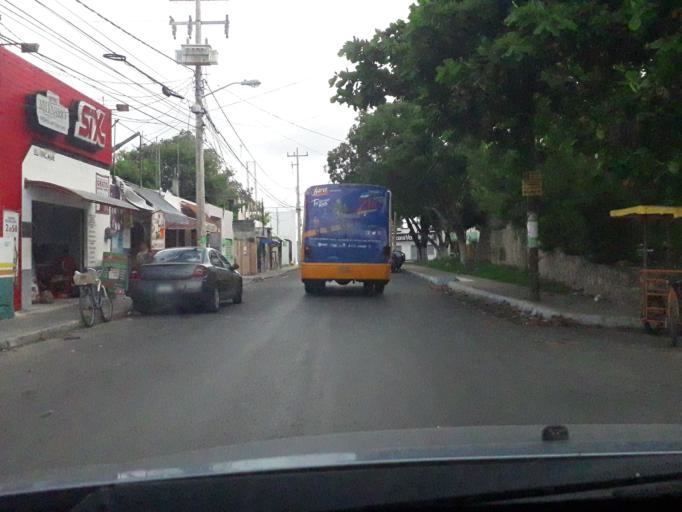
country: MX
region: Yucatan
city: Merida
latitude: 21.0128
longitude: -89.6322
